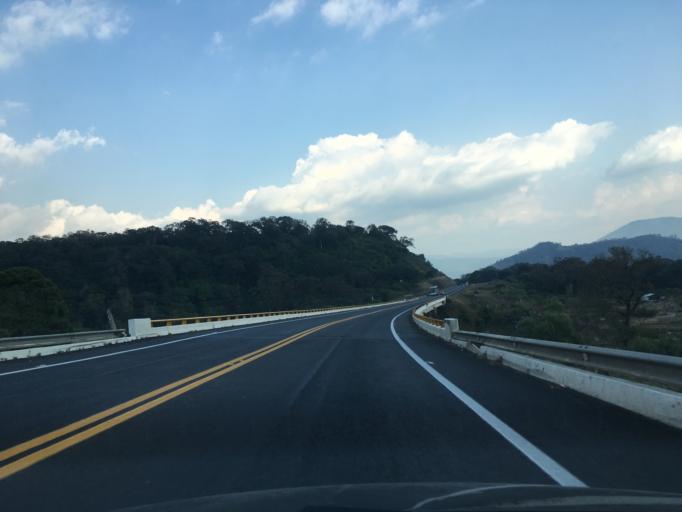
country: MX
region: Michoacan
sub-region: Ziracuaretiro
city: Patuan
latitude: 19.4171
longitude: -101.9587
